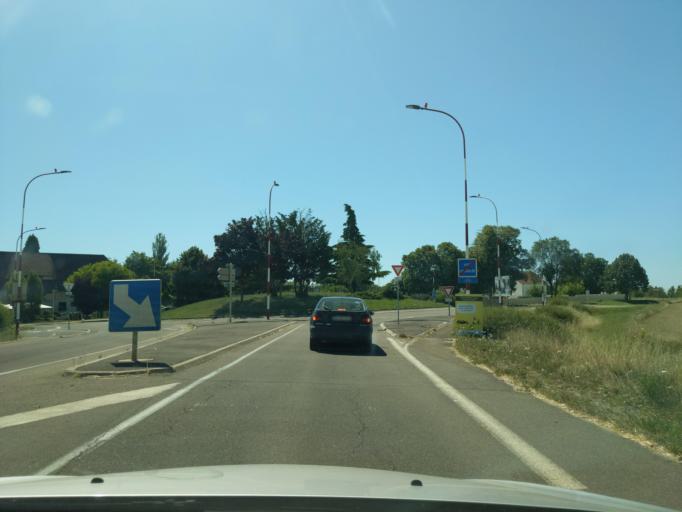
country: FR
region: Bourgogne
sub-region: Departement de la Cote-d'Or
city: Sennecey-les-Dijon
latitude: 47.2891
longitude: 5.0972
